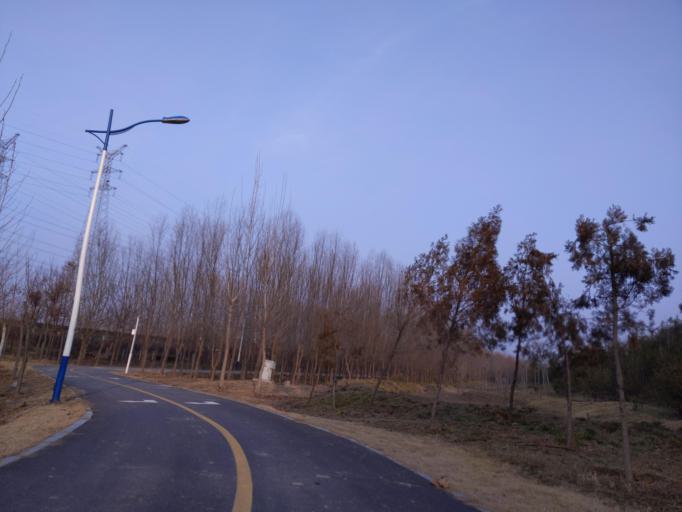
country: CN
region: Henan Sheng
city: Puyang
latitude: 35.8208
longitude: 115.0009
